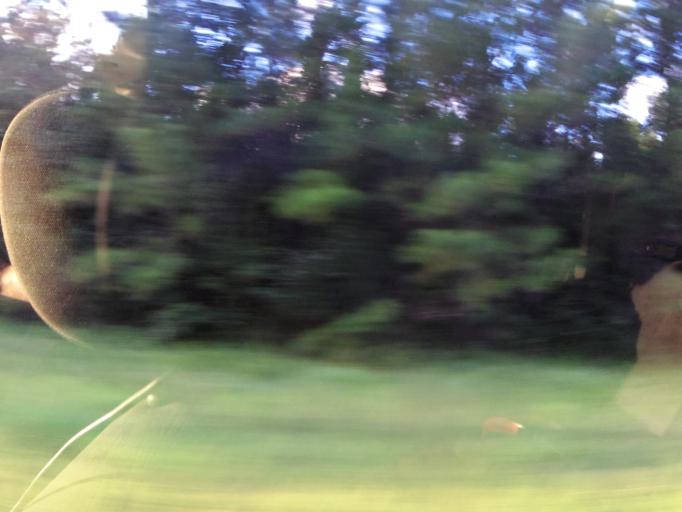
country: US
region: Georgia
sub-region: Camden County
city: Woodbine
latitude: 31.1070
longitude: -81.6602
